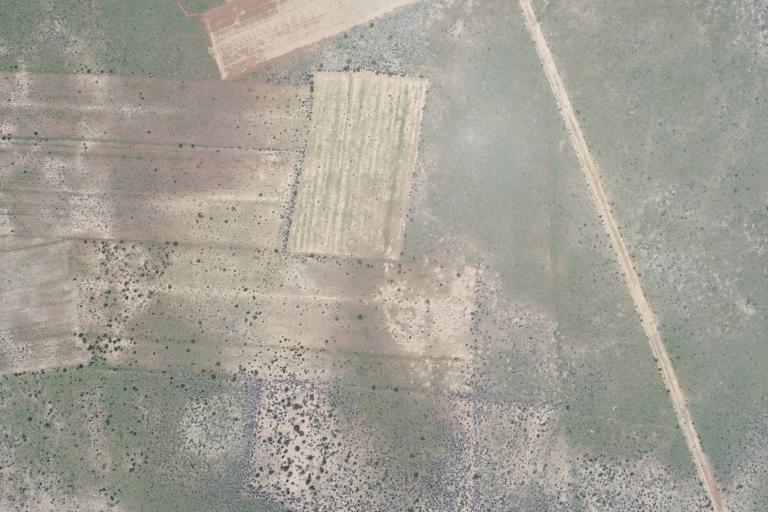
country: BO
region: La Paz
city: Curahuara de Carangas
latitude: -17.3116
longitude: -68.5124
